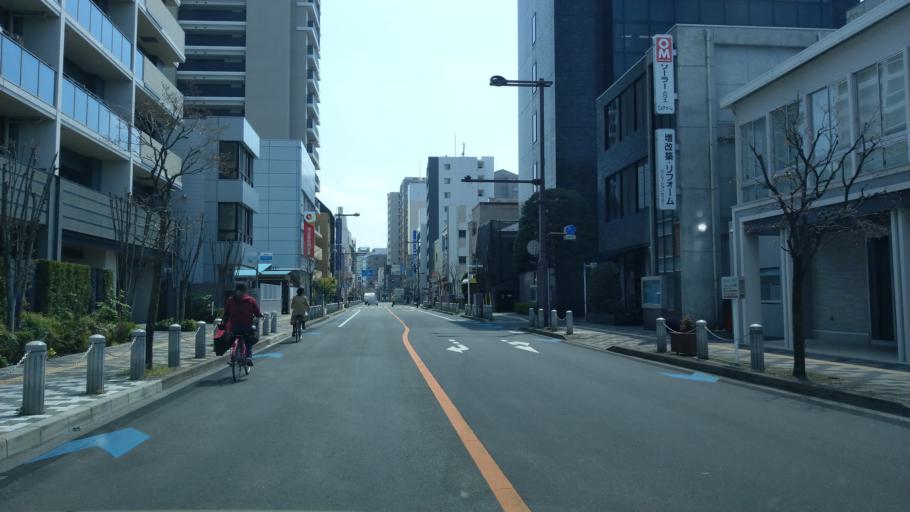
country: JP
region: Saitama
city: Yono
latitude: 35.8743
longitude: 139.6463
